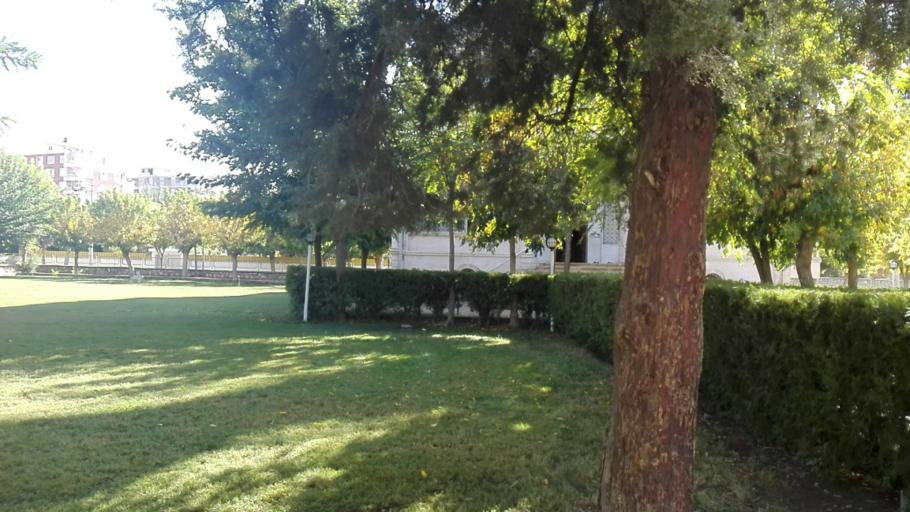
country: TR
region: Batman
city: Batman
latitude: 37.8932
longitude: 41.1250
